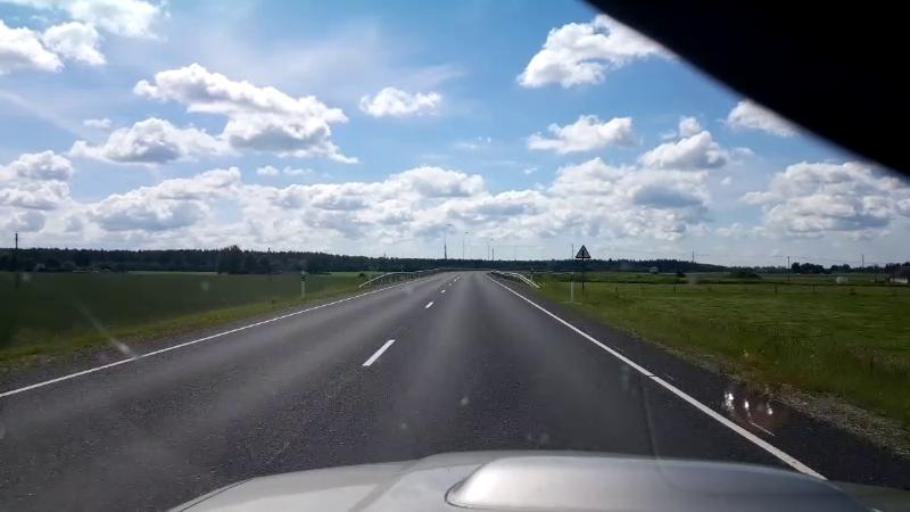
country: EE
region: Jaervamaa
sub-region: Jaerva-Jaani vald
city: Jarva-Jaani
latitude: 59.1443
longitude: 25.7709
